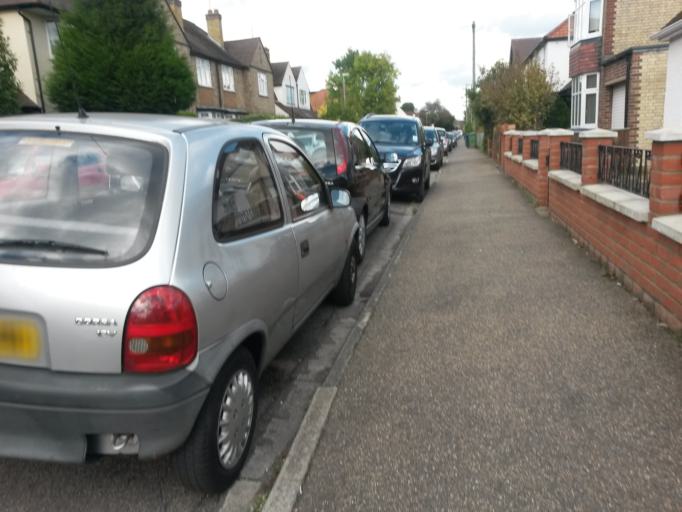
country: GB
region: England
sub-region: Cambridgeshire
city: Cambridge
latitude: 52.2175
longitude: 0.1173
